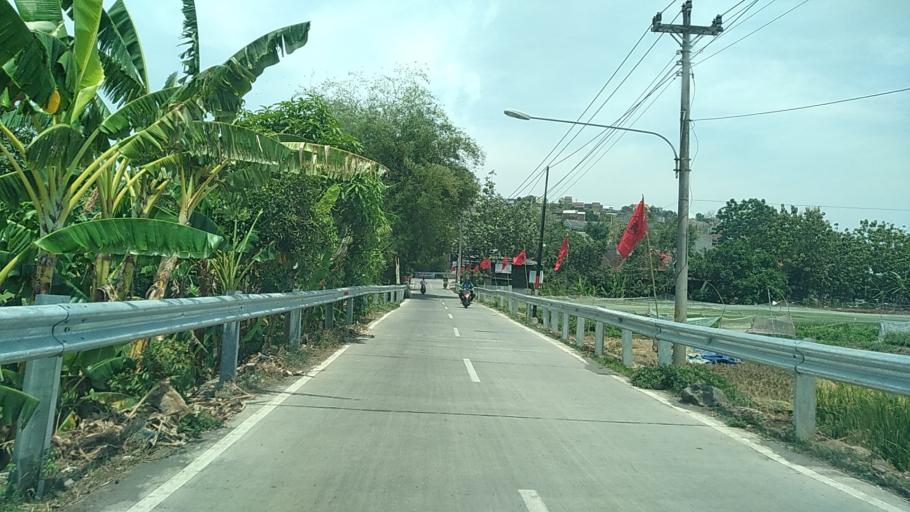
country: ID
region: Central Java
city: Mranggen
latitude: -7.0506
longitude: 110.4727
